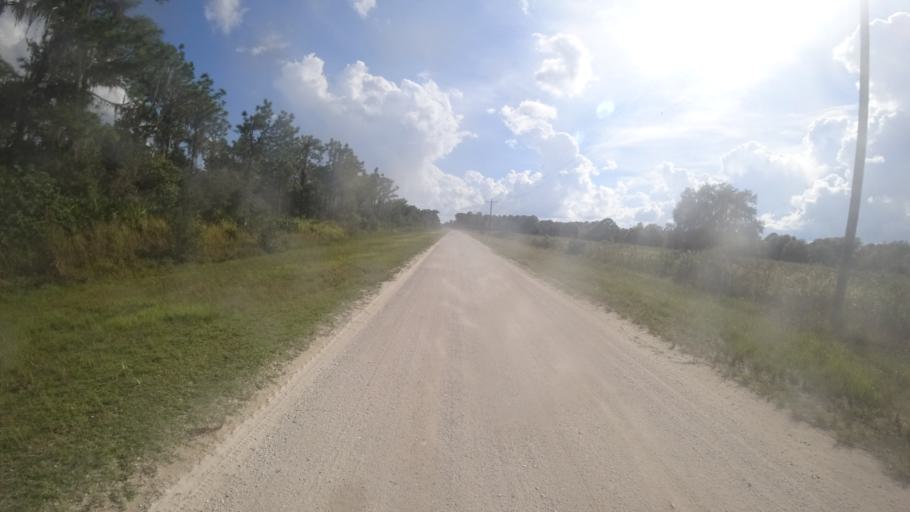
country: US
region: Florida
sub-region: Hillsborough County
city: Balm
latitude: 27.6204
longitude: -82.1197
